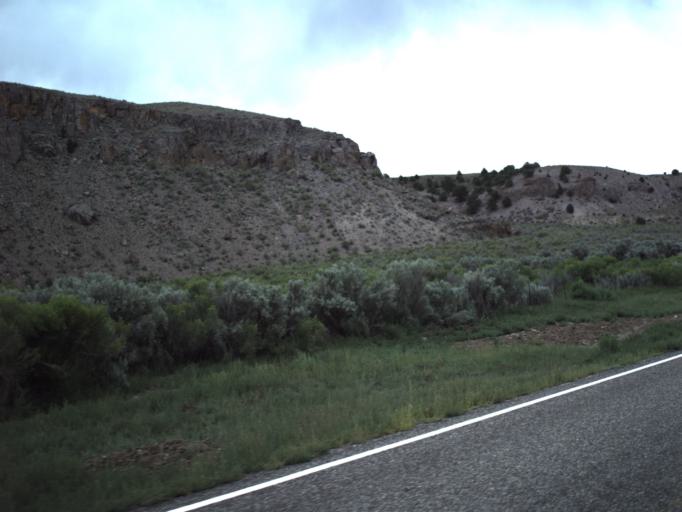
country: US
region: Utah
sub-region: Piute County
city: Junction
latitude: 38.1758
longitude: -112.0658
